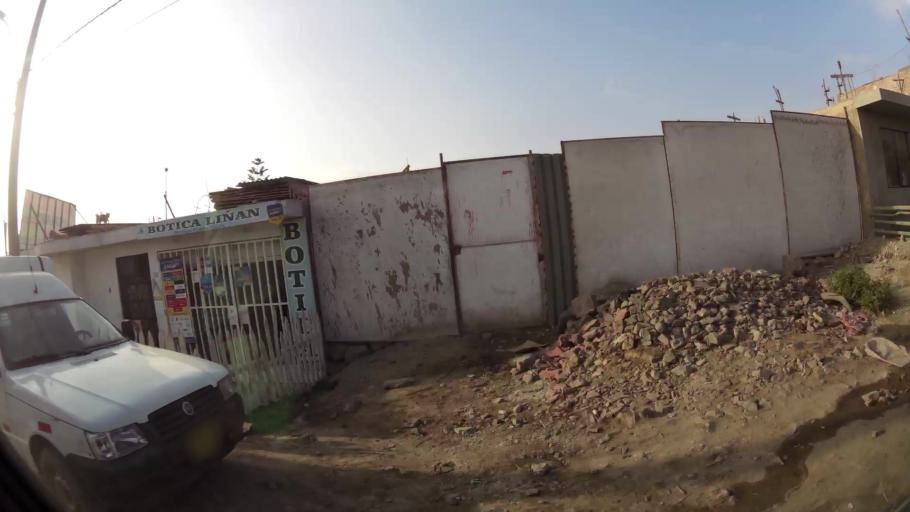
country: PE
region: Lima
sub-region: Lima
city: Santa Rosa
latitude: -11.7693
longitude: -77.1598
